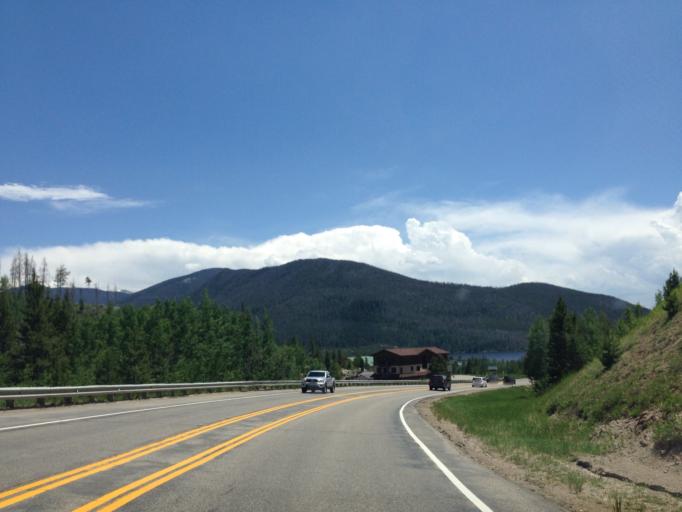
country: US
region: Colorado
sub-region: Grand County
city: Granby
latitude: 40.2551
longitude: -105.8357
